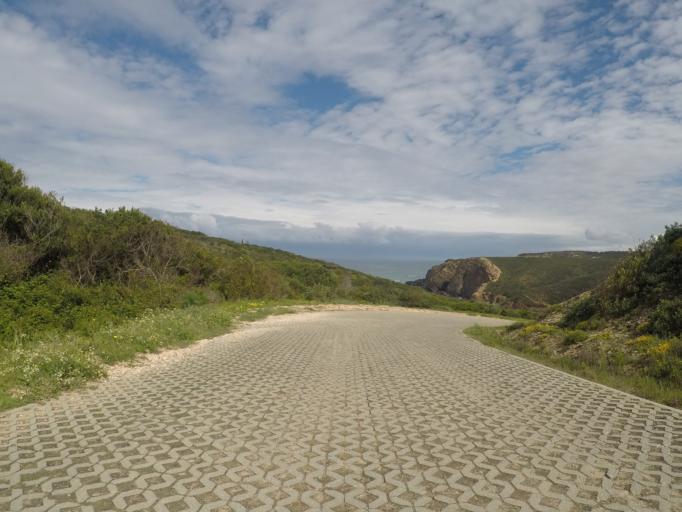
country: PT
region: Beja
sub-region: Odemira
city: Sao Teotonio
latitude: 37.4980
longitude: -8.7909
